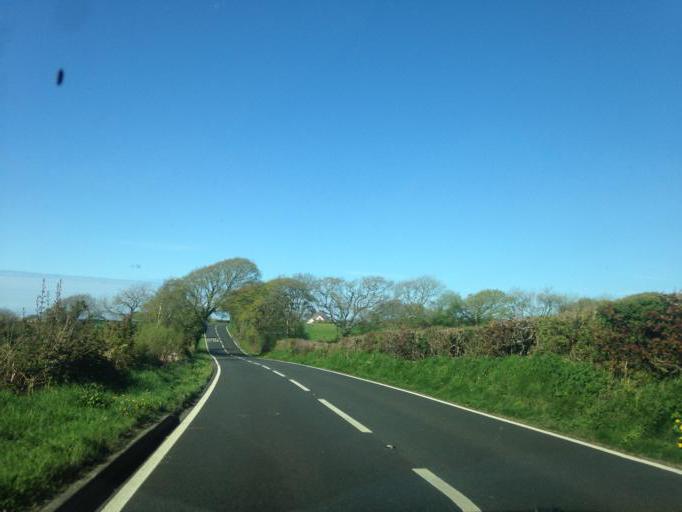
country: GB
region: Wales
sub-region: County of Ceredigion
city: Llanarth
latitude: 52.1995
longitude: -4.3006
